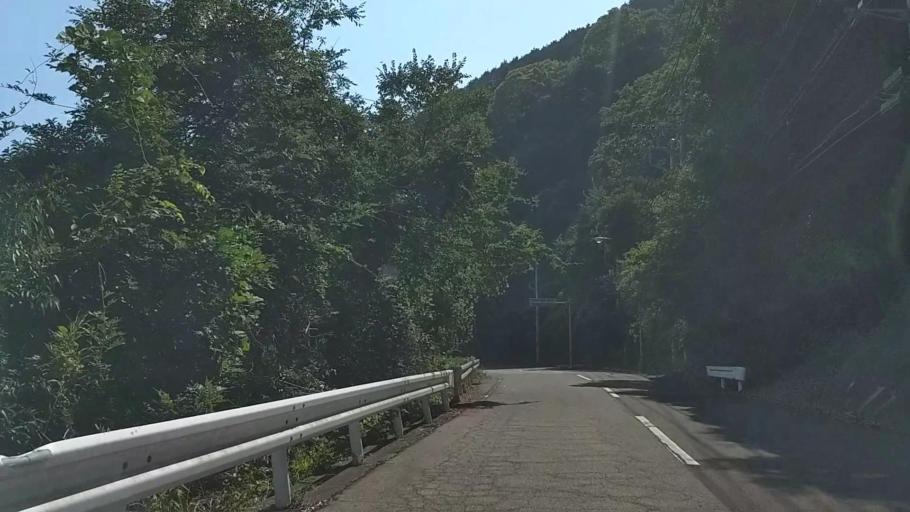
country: JP
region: Yamanashi
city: Ryuo
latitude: 35.4235
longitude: 138.4628
